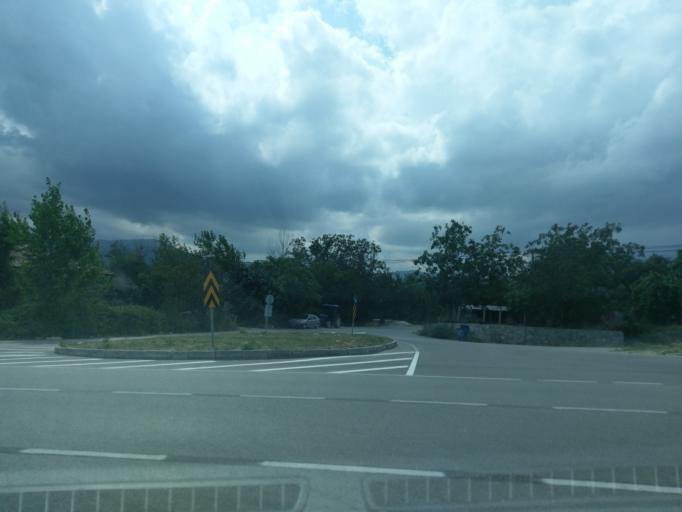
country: TR
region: Sinop
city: Kabali
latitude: 41.8472
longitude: 35.1316
